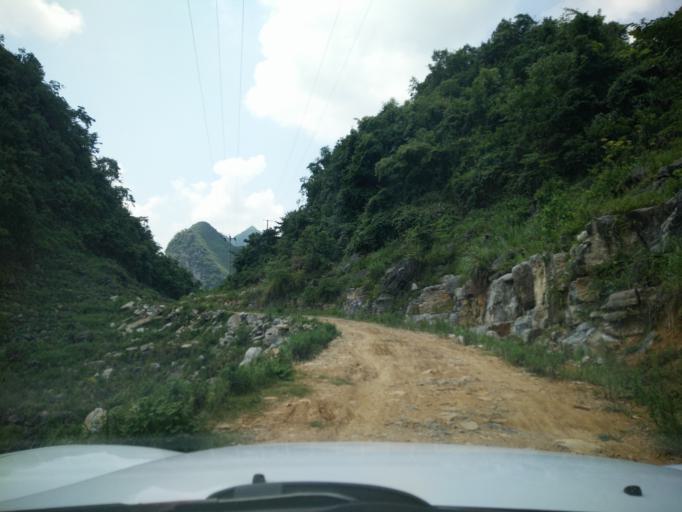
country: CN
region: Guangxi Zhuangzu Zizhiqu
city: Xinzhou
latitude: 25.0059
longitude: 105.7033
